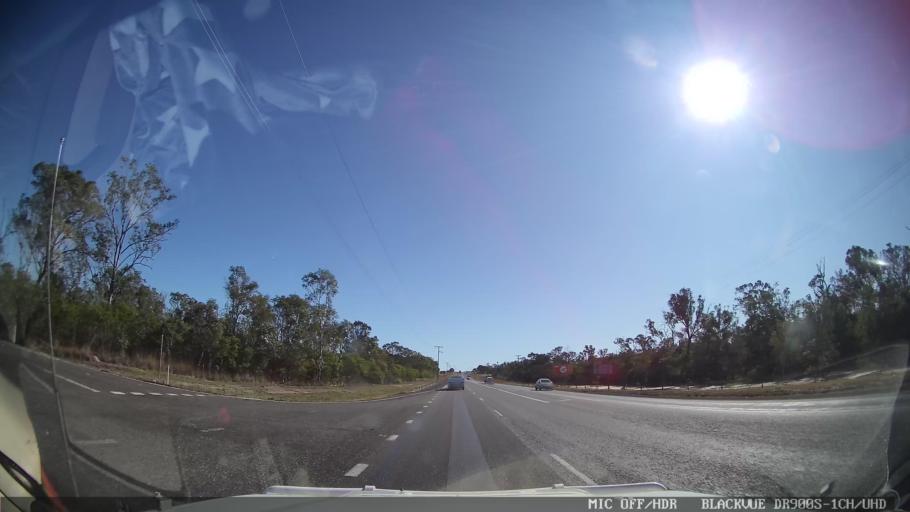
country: AU
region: Queensland
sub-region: Bundaberg
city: Childers
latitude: -25.2488
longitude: 152.3363
